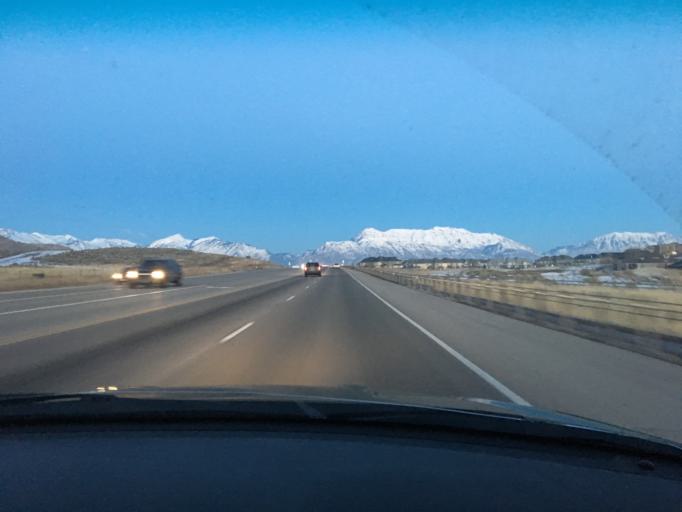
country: US
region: Utah
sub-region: Utah County
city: Saratoga Springs
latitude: 40.3810
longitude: -111.9717
